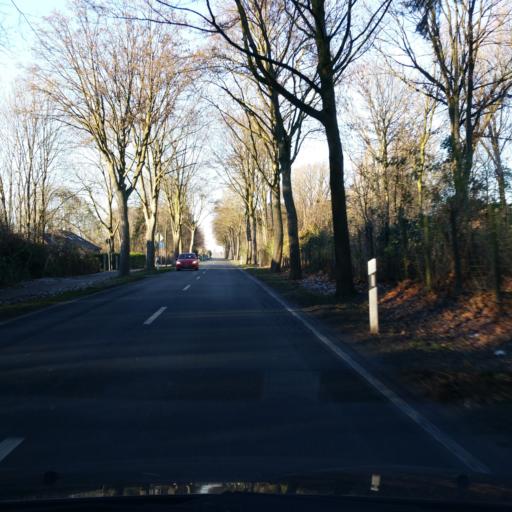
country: DE
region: North Rhine-Westphalia
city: Kalkar
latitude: 51.7334
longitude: 6.3382
